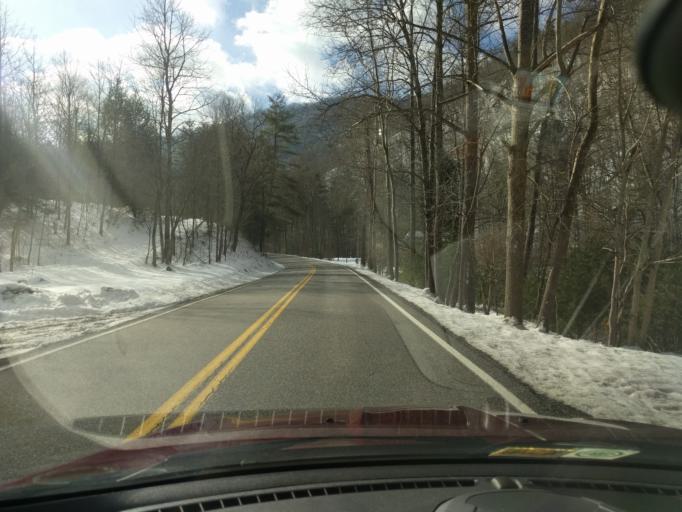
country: US
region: Virginia
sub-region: Bath County
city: Warm Springs
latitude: 38.1184
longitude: -79.9146
